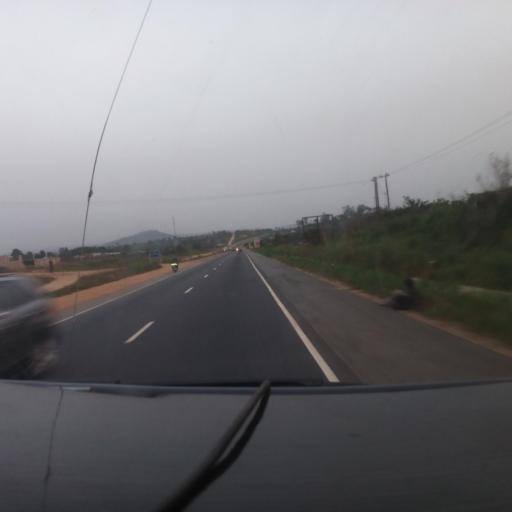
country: GH
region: Eastern
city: Nsawam
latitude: 5.8676
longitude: -0.3656
